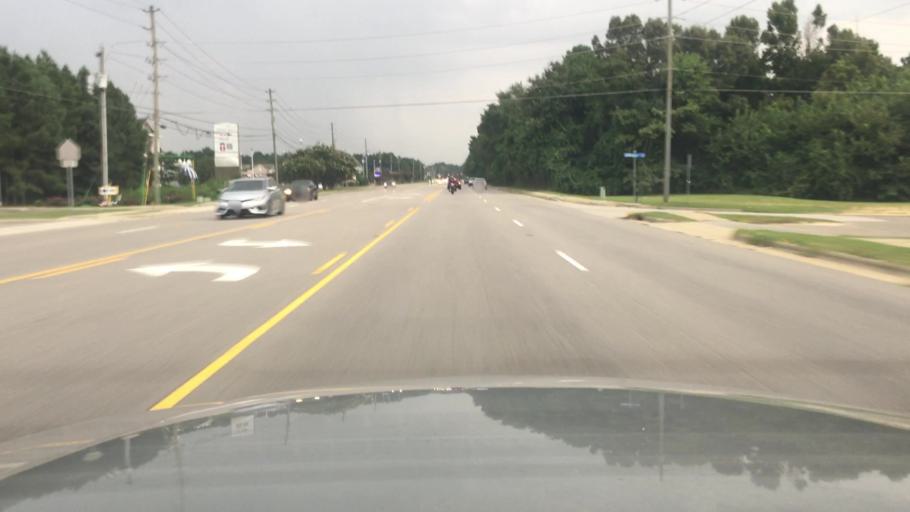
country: US
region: North Carolina
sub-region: Cumberland County
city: Fort Bragg
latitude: 35.0901
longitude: -79.0107
